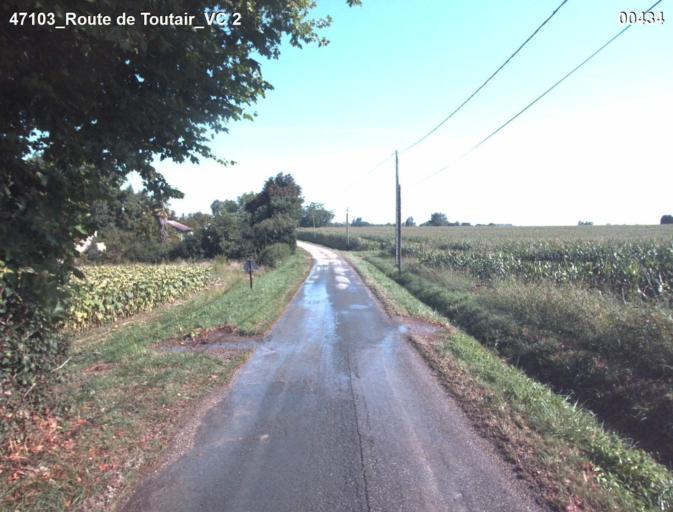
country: FR
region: Aquitaine
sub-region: Departement du Lot-et-Garonne
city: Nerac
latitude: 44.0814
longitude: 0.3218
